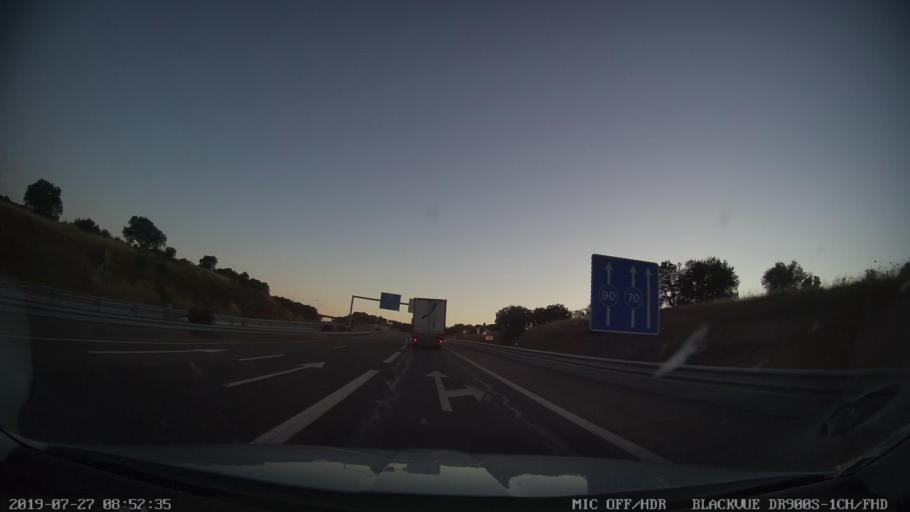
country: PT
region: Portalegre
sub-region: Elvas
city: Elvas
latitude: 38.9107
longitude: -7.1737
